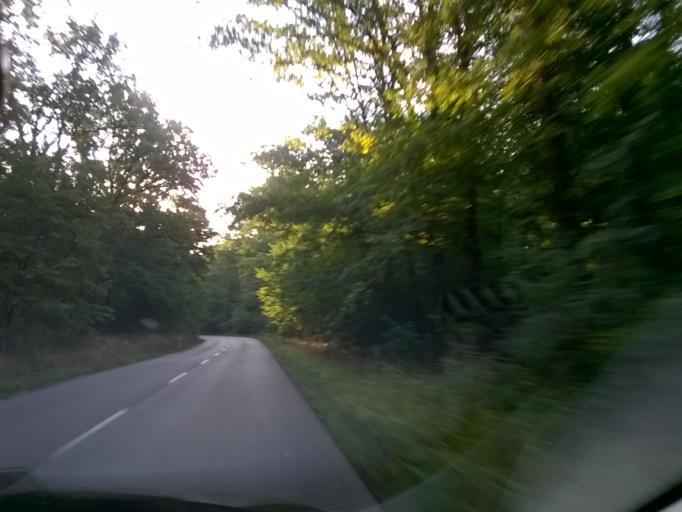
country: SK
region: Nitriansky
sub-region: Okres Nitra
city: Nitra
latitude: 48.2829
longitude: 17.9814
